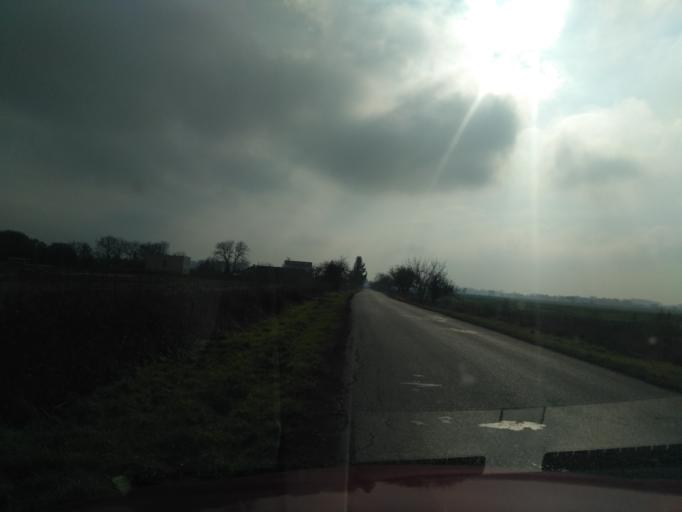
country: SK
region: Kosicky
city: Kosice
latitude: 48.6669
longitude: 21.3494
